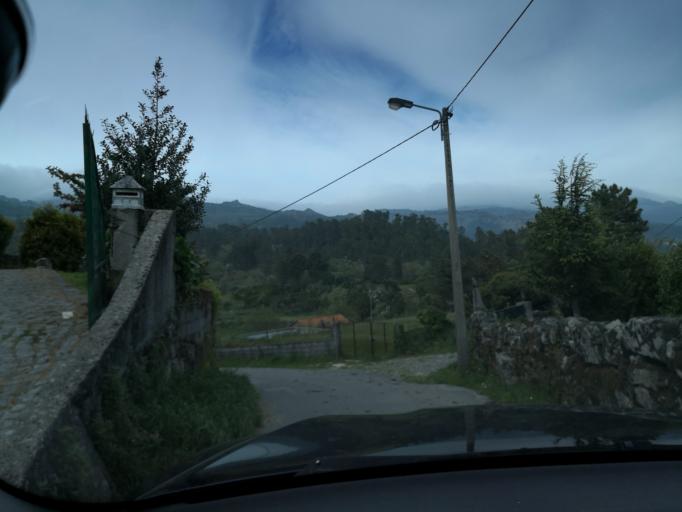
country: PT
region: Vila Real
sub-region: Vila Real
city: Vila Real
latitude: 41.3038
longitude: -7.8002
